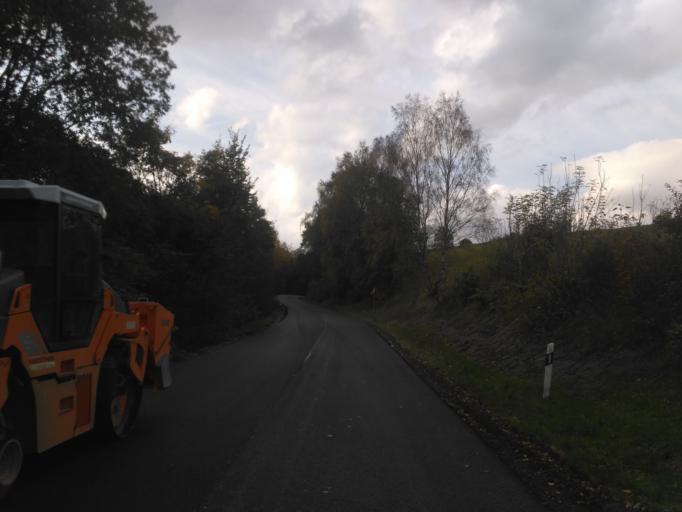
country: DE
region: Saxony
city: Rathmannsdorf
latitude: 50.9801
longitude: 14.1746
